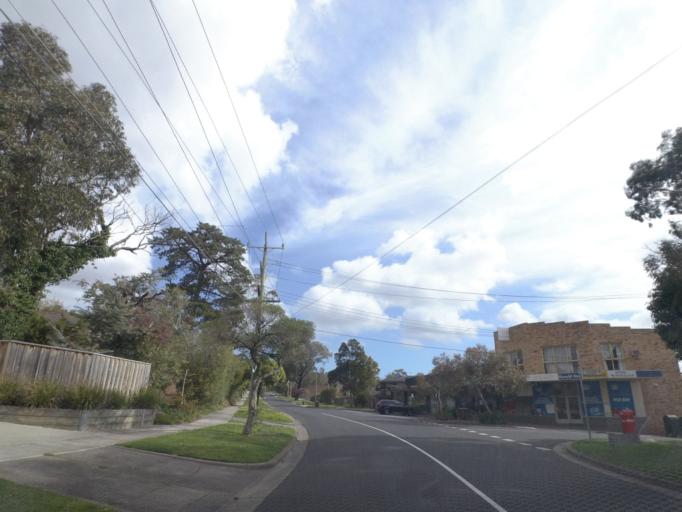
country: AU
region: Victoria
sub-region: Whitehorse
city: Vermont
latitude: -37.8383
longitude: 145.2073
